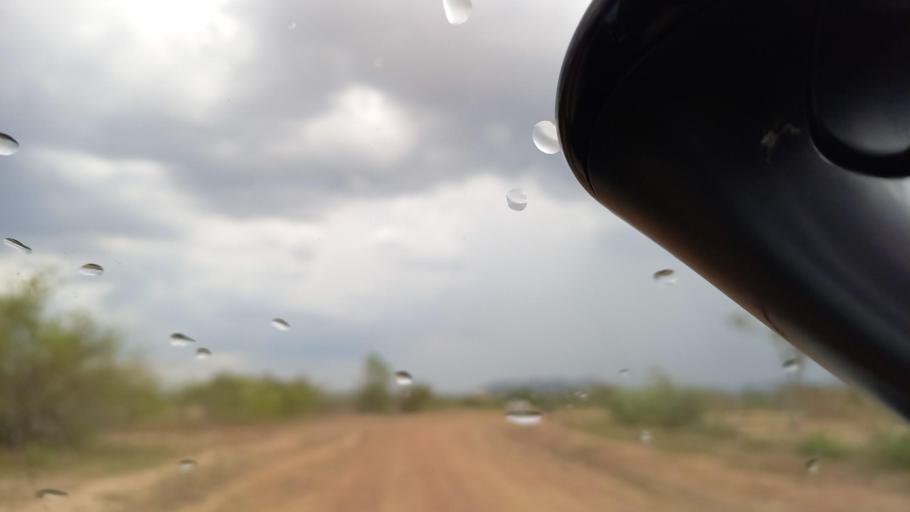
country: ZM
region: Lusaka
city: Kafue
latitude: -15.8543
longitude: 28.1136
